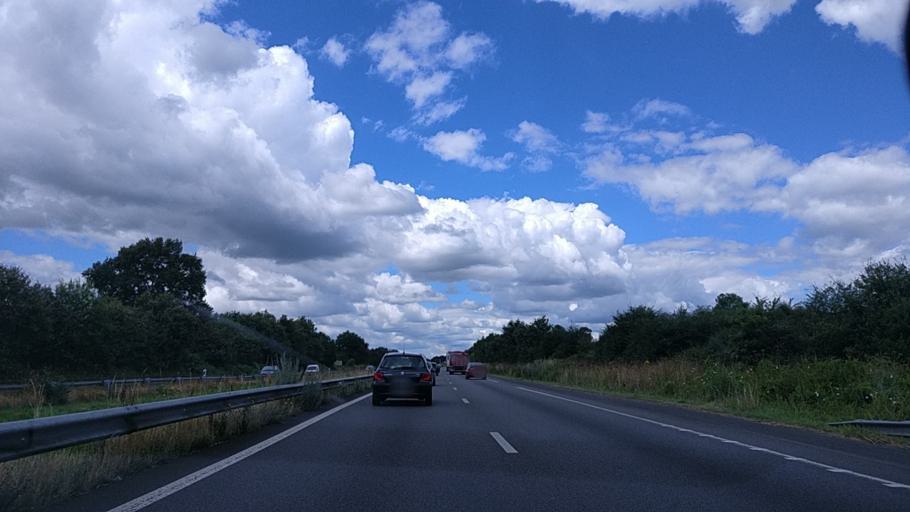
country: FR
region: Pays de la Loire
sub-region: Departement de la Loire-Atlantique
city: Sautron
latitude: 47.2698
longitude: -1.7141
